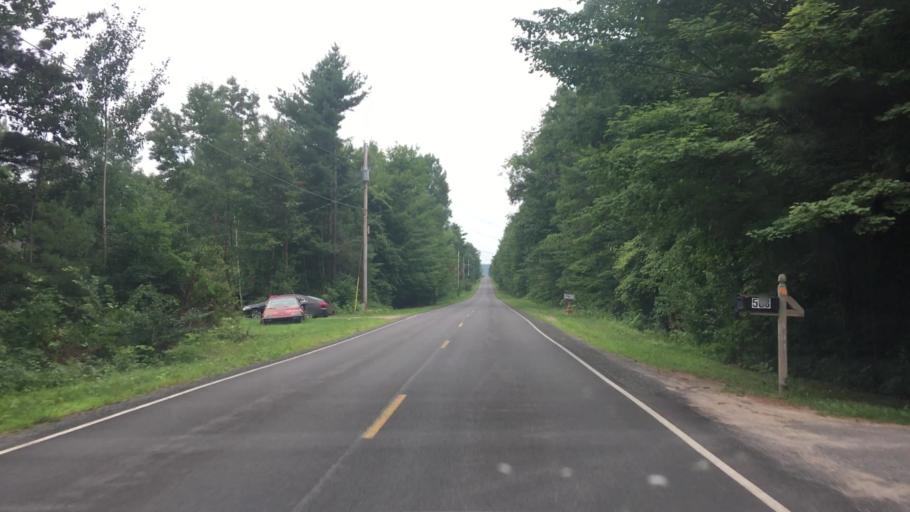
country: US
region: New York
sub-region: Clinton County
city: Peru
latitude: 44.5968
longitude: -73.6274
